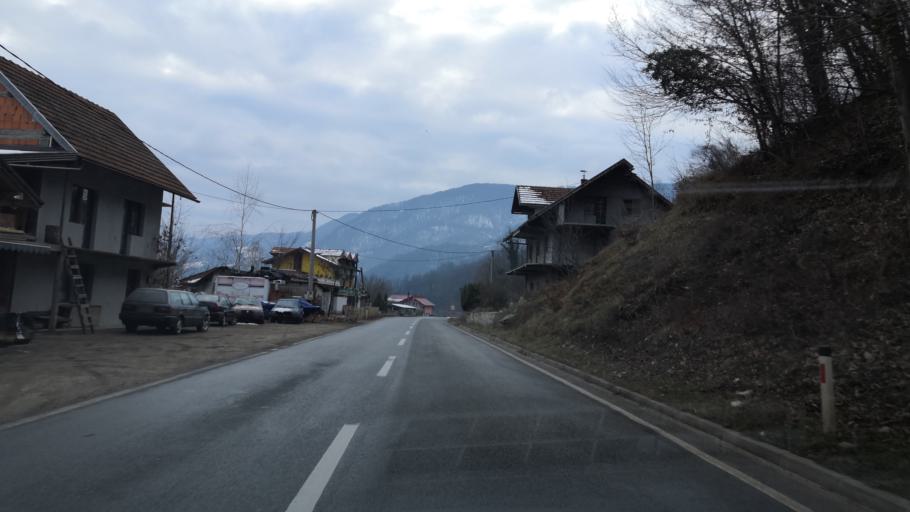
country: RS
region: Central Serbia
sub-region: Macvanski Okrug
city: Mali Zvornik
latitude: 44.3294
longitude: 19.1281
